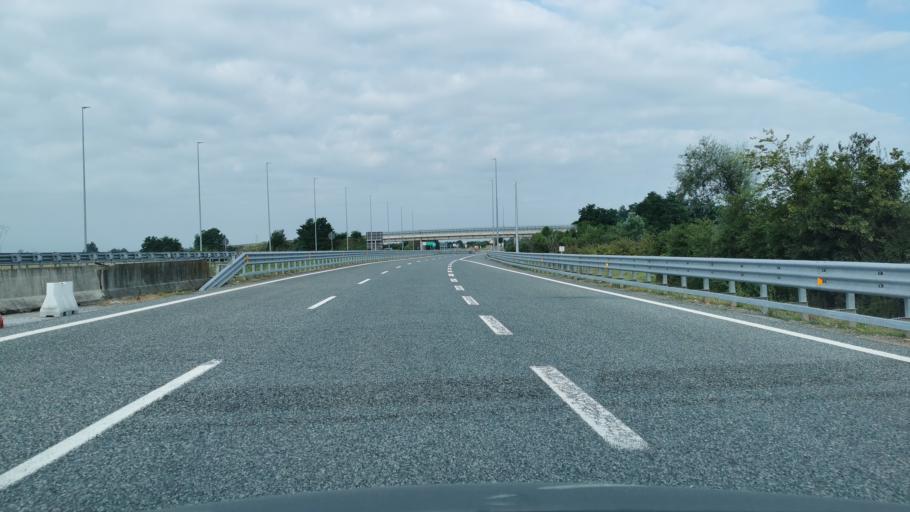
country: IT
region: Piedmont
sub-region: Provincia di Cuneo
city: Magliano Alpi
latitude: 44.4845
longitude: 7.8131
